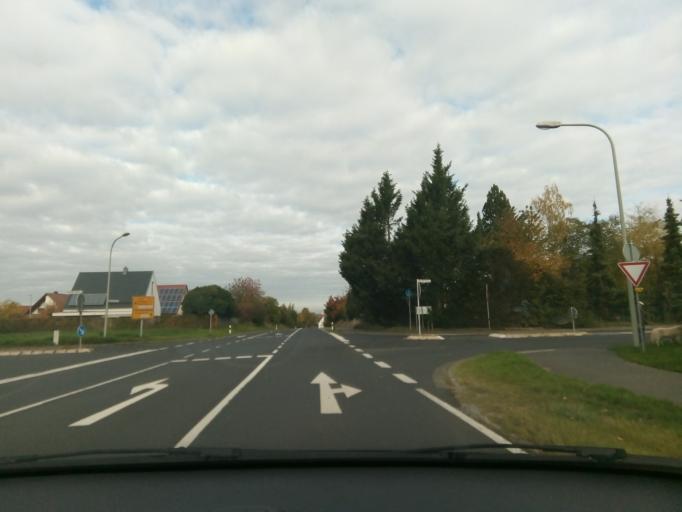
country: DE
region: Bavaria
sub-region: Regierungsbezirk Unterfranken
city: Gerolzhofen
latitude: 49.8929
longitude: 10.3559
